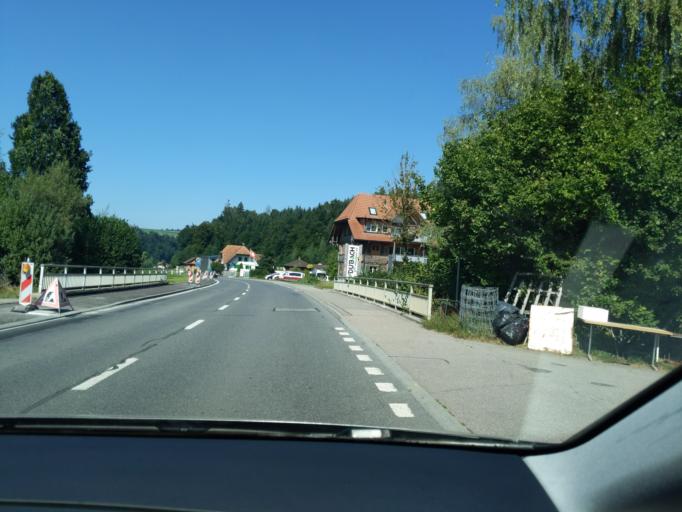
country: CH
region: Lucerne
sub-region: Willisau District
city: Zell
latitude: 47.1289
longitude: 7.9095
